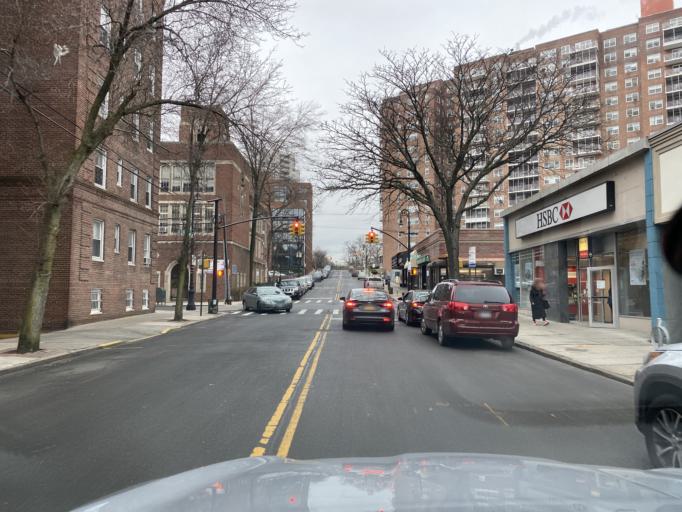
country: US
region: New York
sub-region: New York County
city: Inwood
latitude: 40.8858
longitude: -73.9105
